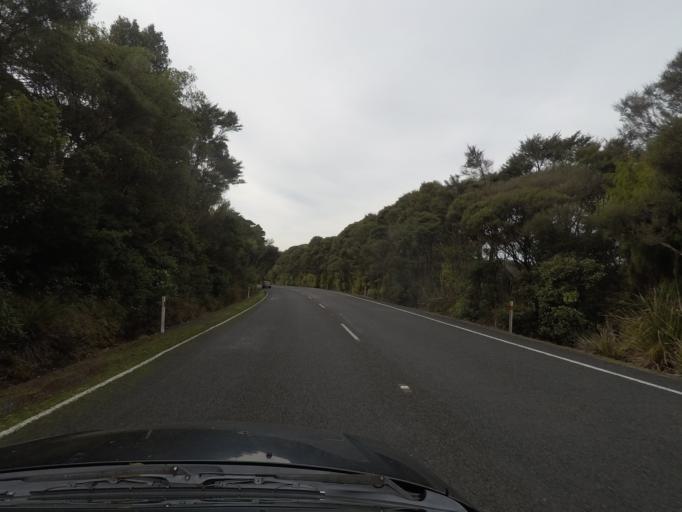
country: NZ
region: Auckland
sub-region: Auckland
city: Titirangi
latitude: -36.9423
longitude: 174.5518
